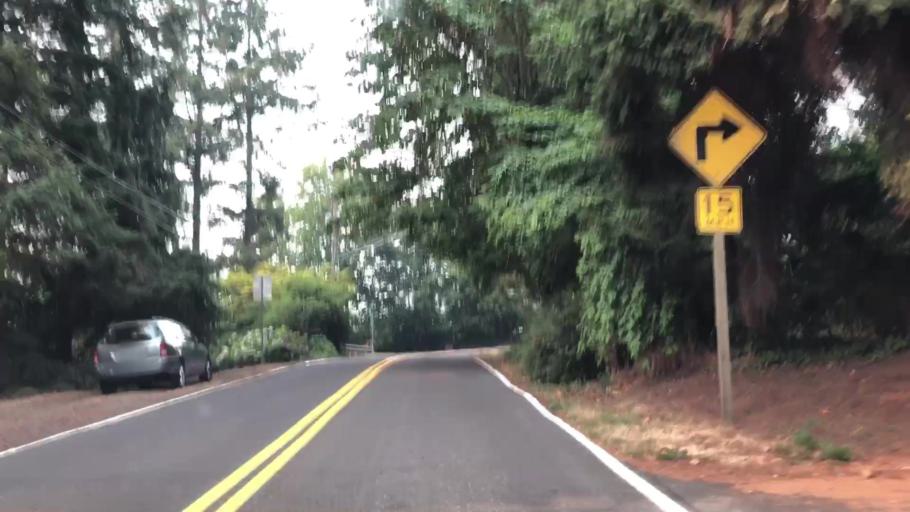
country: US
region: Washington
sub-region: King County
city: Kenmore
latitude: 47.7800
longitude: -122.2430
